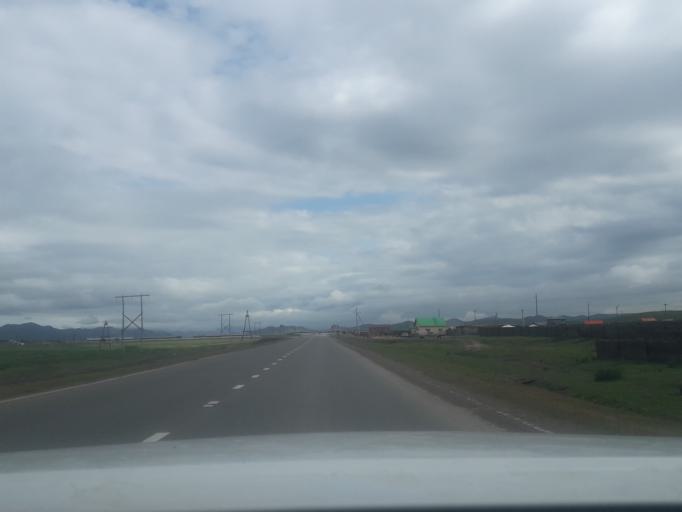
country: MN
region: Central Aimak
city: Altanbulag
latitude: 47.7668
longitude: 106.5988
